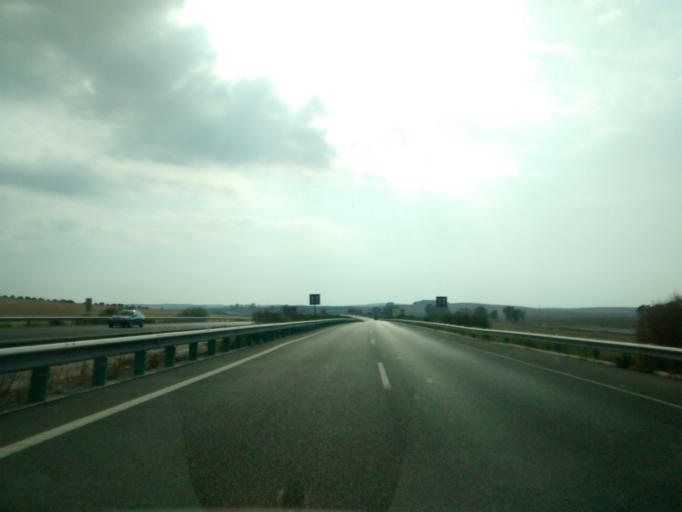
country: ES
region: Andalusia
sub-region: Provincia de Cadiz
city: Arcos de la Frontera
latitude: 36.7408
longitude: -5.8780
